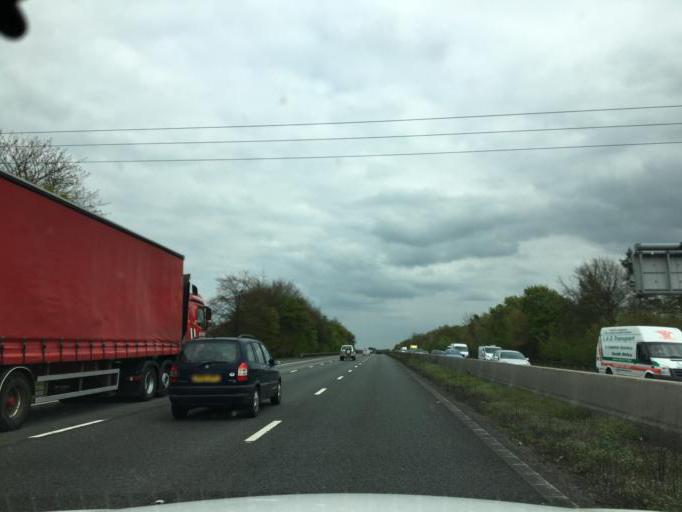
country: GB
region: England
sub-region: Wiltshire
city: Nettleton
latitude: 51.5142
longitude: -2.2346
